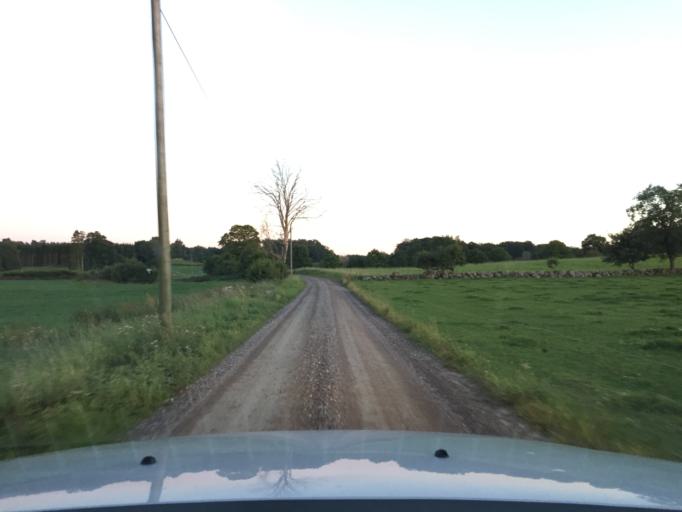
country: SE
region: Skane
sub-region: Hassleholms Kommun
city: Sosdala
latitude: 55.9818
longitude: 13.6790
